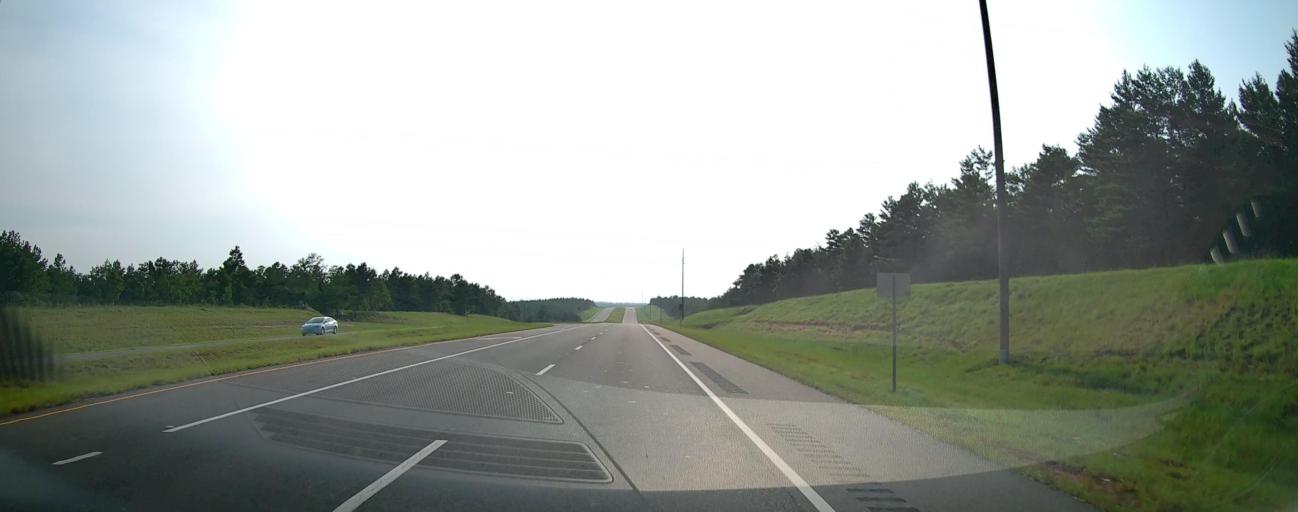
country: US
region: Georgia
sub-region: Talbot County
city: Talbotton
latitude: 32.5947
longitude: -84.4129
